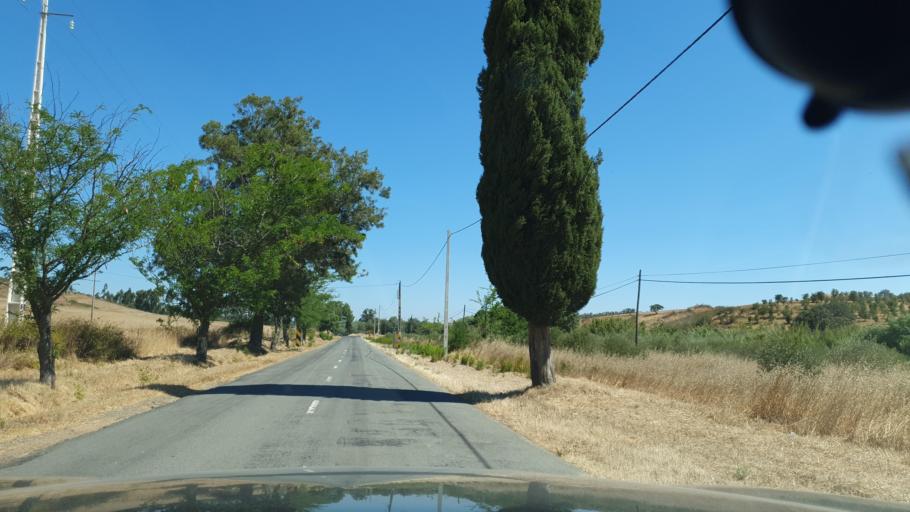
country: PT
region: Faro
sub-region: Monchique
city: Monchique
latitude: 37.4501
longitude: -8.4870
